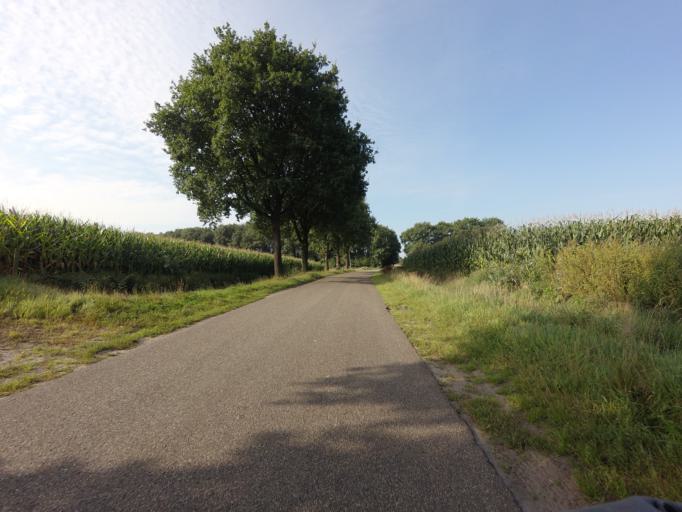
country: NL
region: Friesland
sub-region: Gemeente Weststellingwerf
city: Noordwolde
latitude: 52.9237
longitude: 6.1732
